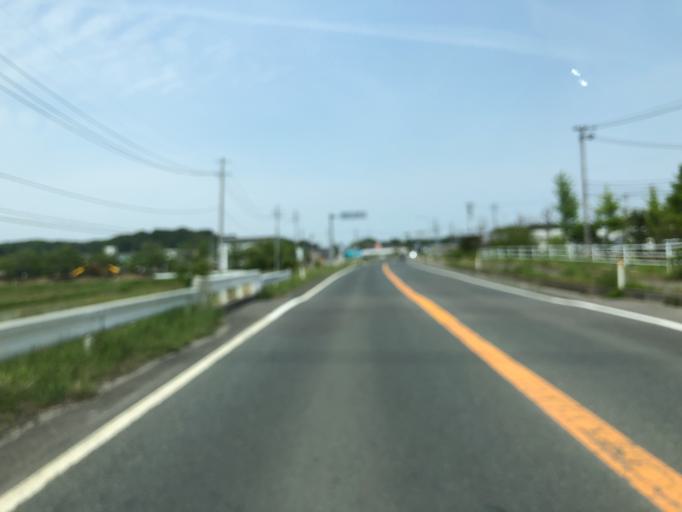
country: JP
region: Miyagi
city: Marumori
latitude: 37.8420
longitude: 140.9183
